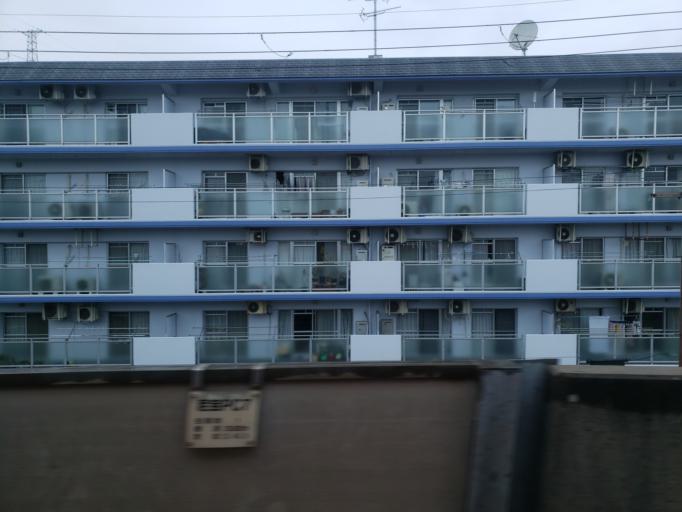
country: JP
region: Hyogo
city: Amagasaki
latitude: 34.7168
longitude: 135.3894
